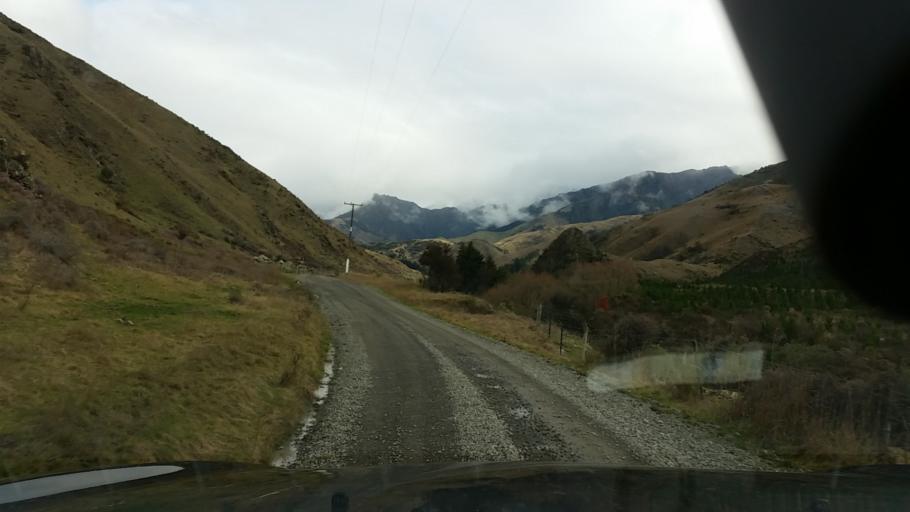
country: NZ
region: Tasman
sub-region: Tasman District
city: Richmond
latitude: -41.7296
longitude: 173.4439
